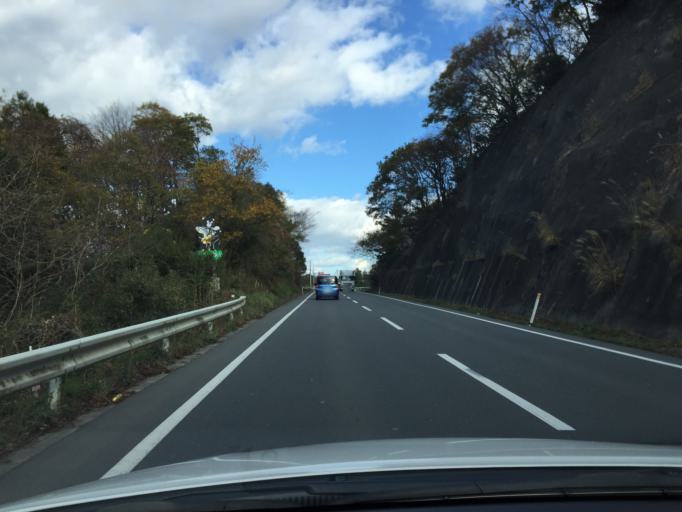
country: JP
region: Fukushima
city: Namie
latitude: 37.3780
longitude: 141.0089
